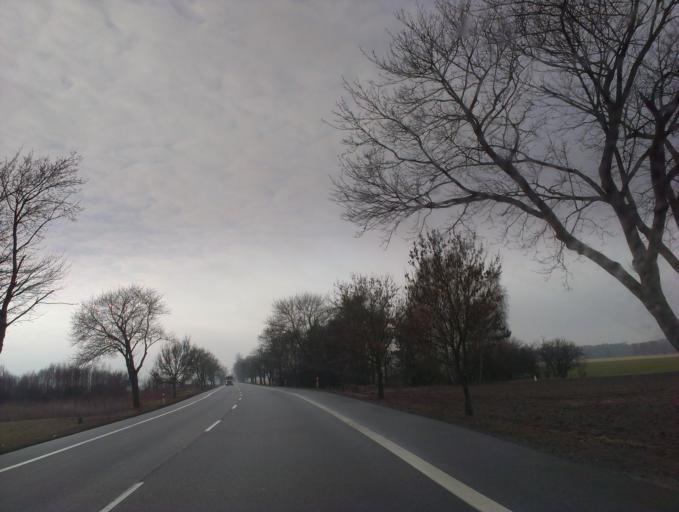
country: PL
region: Greater Poland Voivodeship
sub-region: Powiat pilski
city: Ujscie
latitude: 53.0940
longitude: 16.7400
